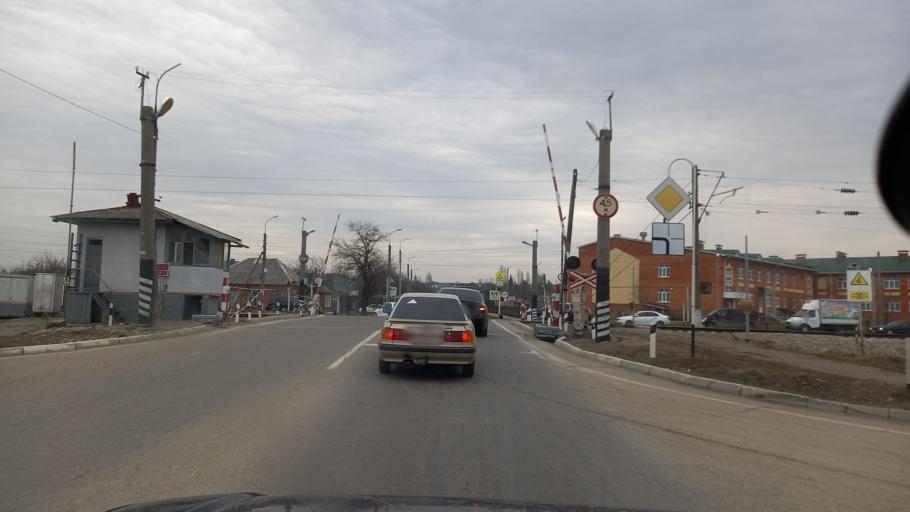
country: RU
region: Adygeya
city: Maykop
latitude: 44.5982
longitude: 40.1321
